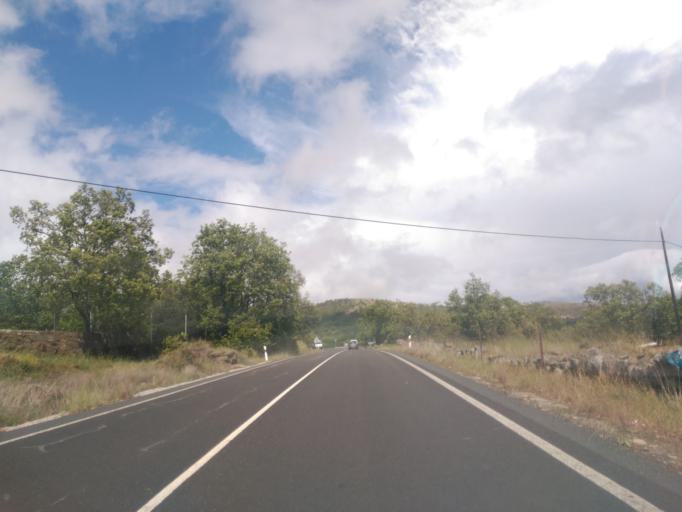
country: ES
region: Castille and Leon
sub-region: Provincia de Salamanca
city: Vallejera de Riofrio
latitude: 40.4036
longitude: -5.7262
